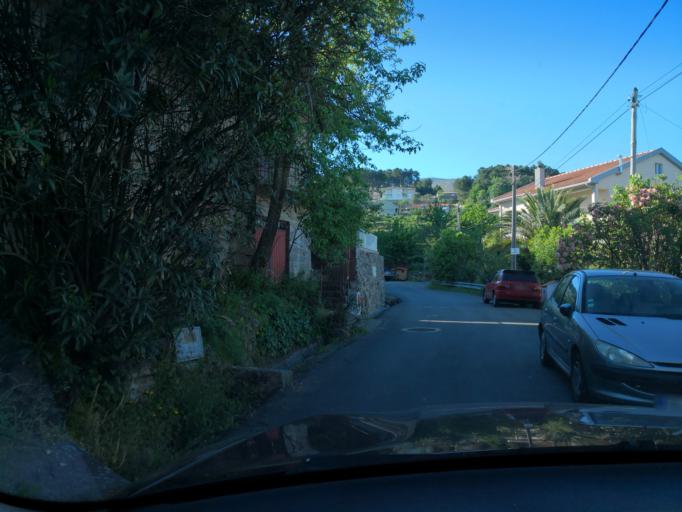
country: PT
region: Vila Real
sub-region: Vila Real
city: Vila Real
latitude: 41.3283
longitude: -7.7473
